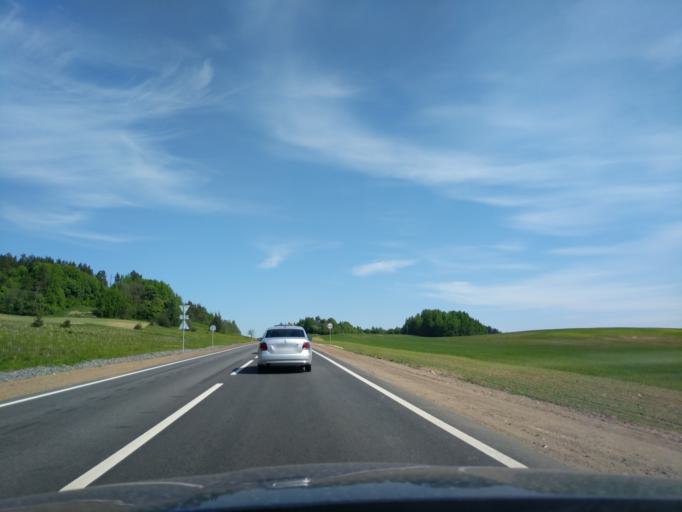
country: BY
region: Minsk
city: Bal'shavik
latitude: 54.0909
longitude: 27.5350
